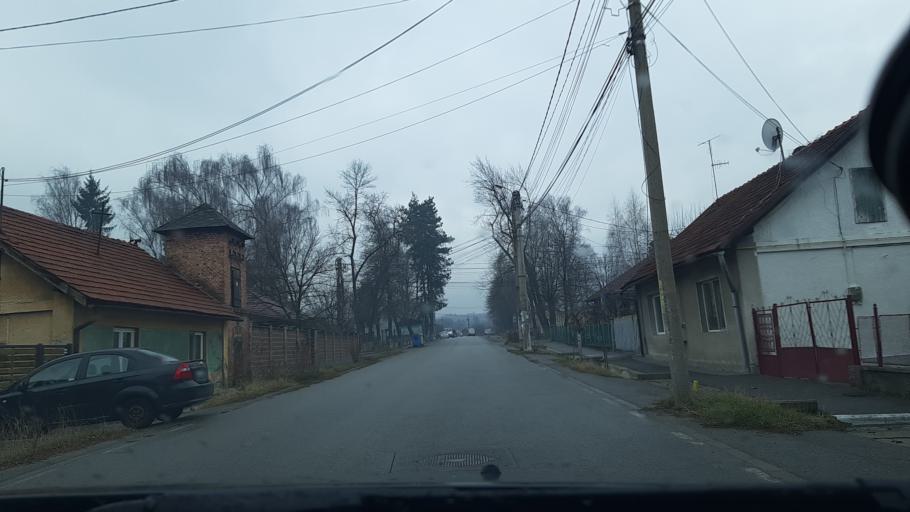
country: RO
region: Hunedoara
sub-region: Oras Petrila
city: Petrila
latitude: 45.4430
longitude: 23.4118
